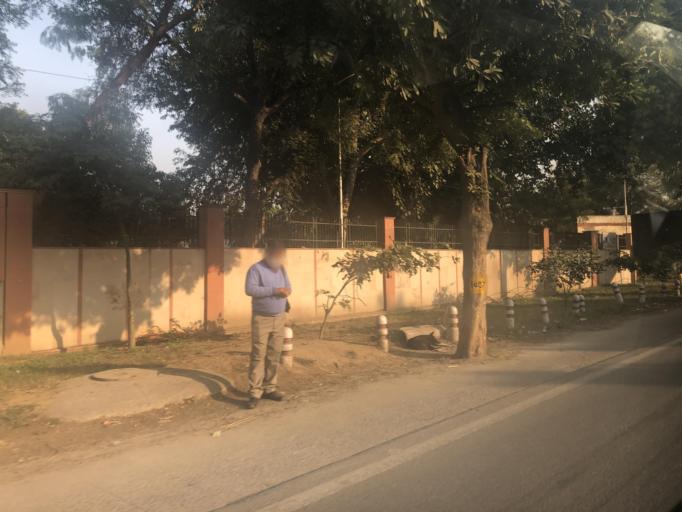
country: IN
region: Haryana
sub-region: Gurgaon
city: Gurgaon
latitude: 28.5547
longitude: 77.0062
